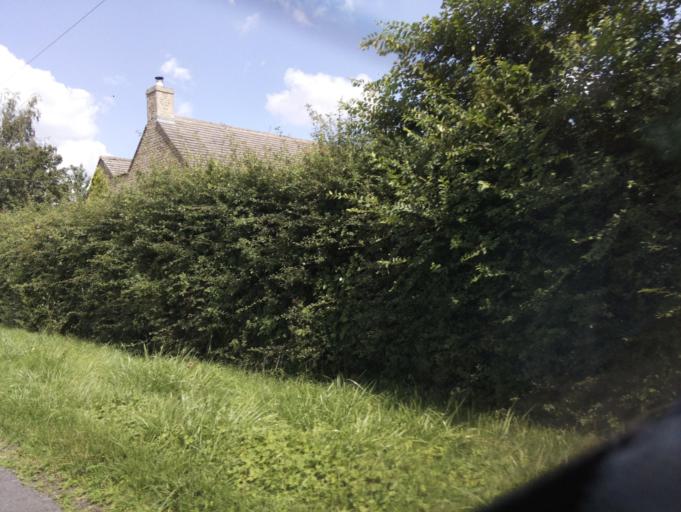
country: GB
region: England
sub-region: Wiltshire
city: Minety
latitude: 51.6034
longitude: -1.9477
